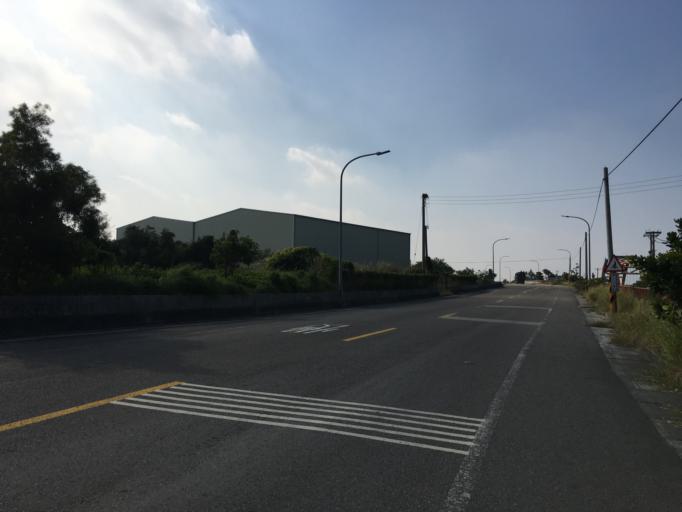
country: TW
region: Taiwan
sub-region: Hsinchu
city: Hsinchu
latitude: 24.8033
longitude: 120.9176
